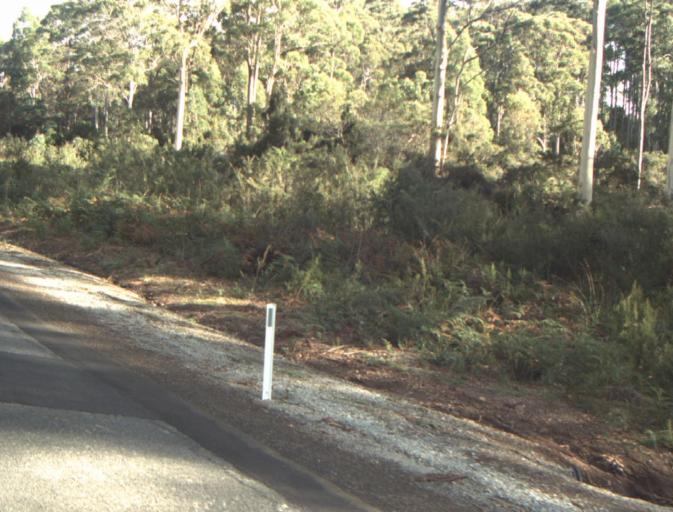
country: AU
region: Tasmania
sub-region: Launceston
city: Mayfield
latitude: -41.3063
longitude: 147.1989
